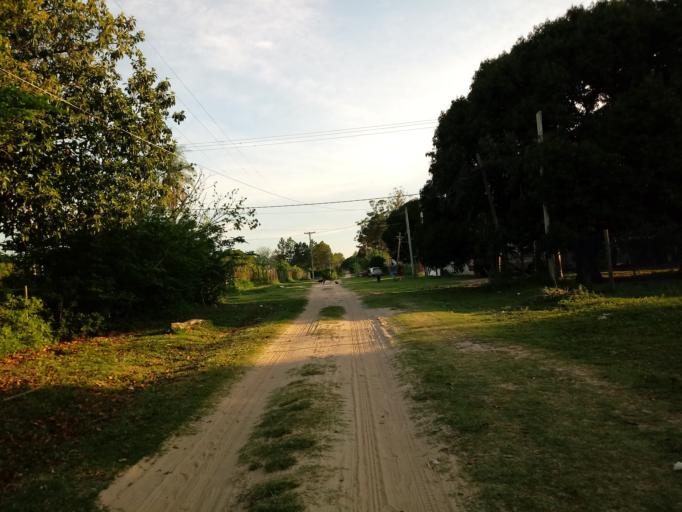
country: AR
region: Corrientes
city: San Luis del Palmar
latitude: -27.4517
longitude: -58.6572
